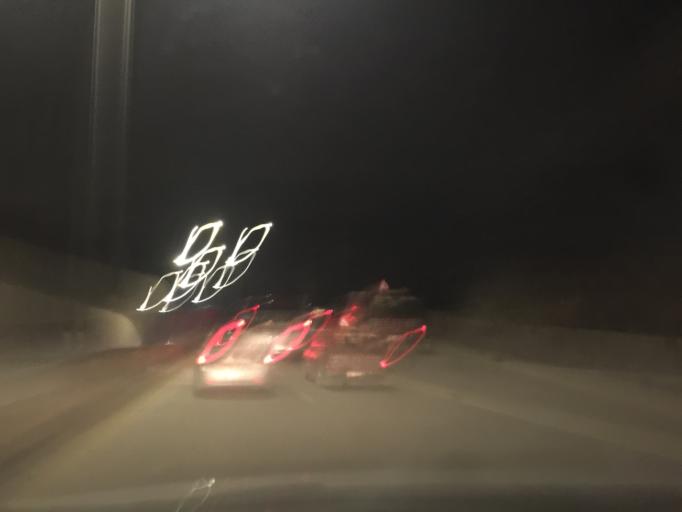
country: JO
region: Amman
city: Umm as Summaq
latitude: 31.8849
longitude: 35.8430
